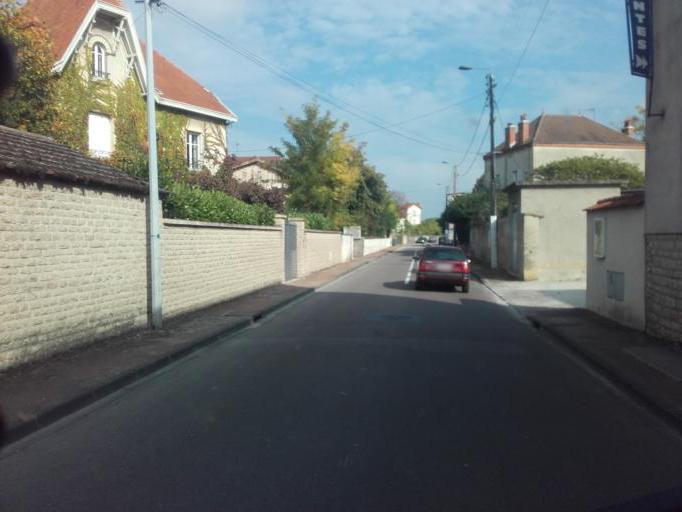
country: FR
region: Bourgogne
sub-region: Departement de la Cote-d'Or
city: Beaune
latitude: 47.0262
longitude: 4.8487
